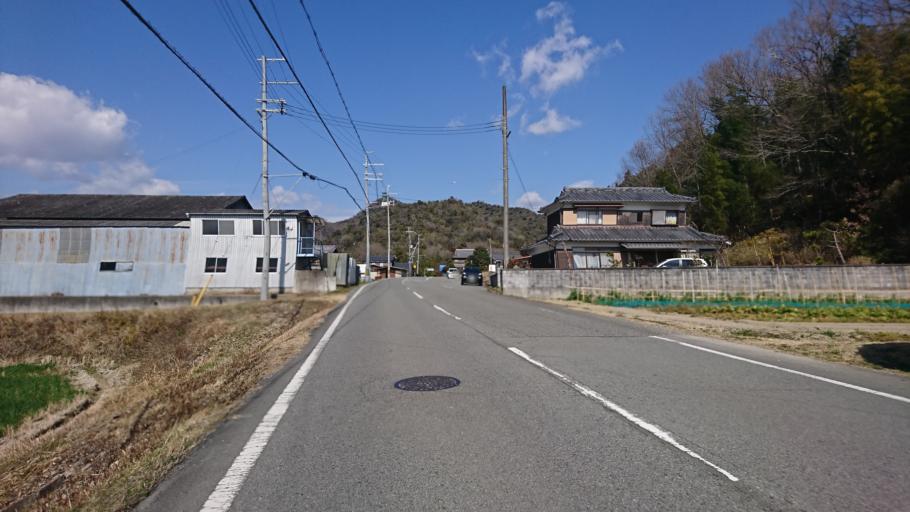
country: JP
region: Hyogo
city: Kakogawacho-honmachi
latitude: 34.8518
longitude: 134.8102
